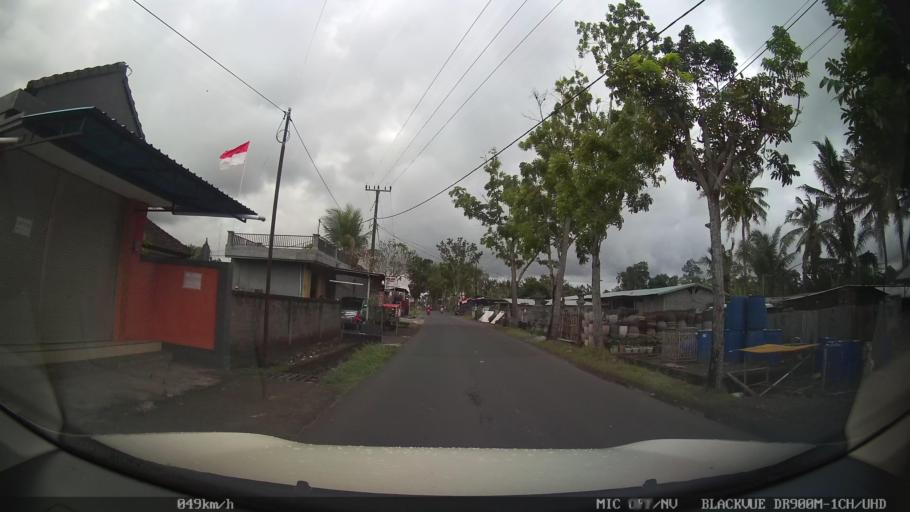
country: ID
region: Bali
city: Banjar Cemenggon
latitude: -8.5577
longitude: 115.1896
